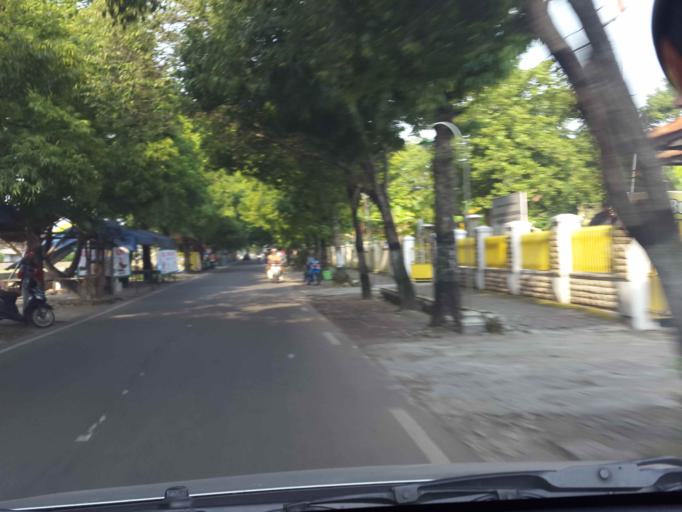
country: ID
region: Central Java
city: Sragen
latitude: -7.4285
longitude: 111.0247
